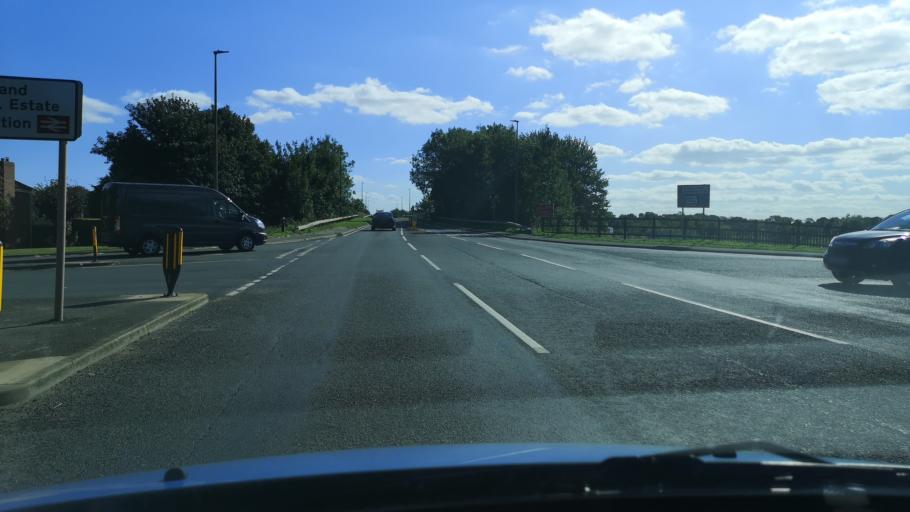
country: GB
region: England
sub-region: North Lincolnshire
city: Crowle
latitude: 53.5921
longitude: -0.8189
